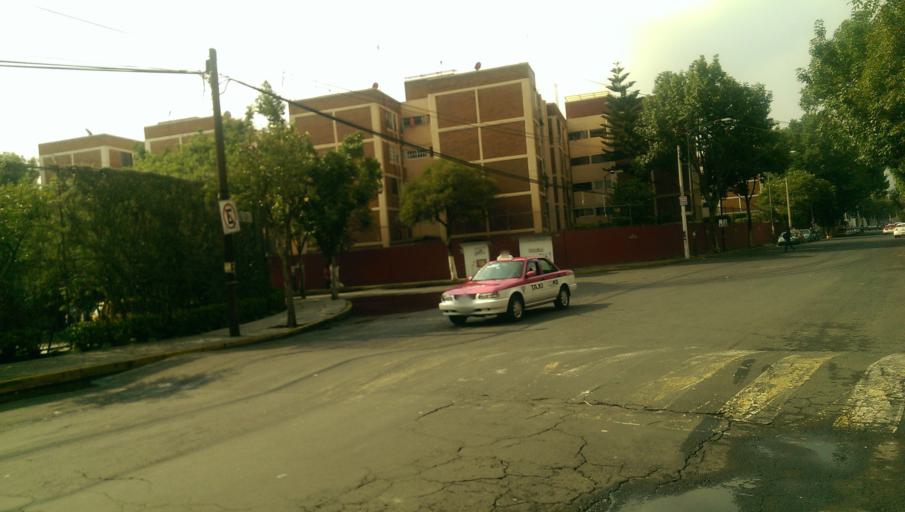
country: MX
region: Mexico City
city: Tlalpan
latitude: 19.2874
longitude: -99.1359
